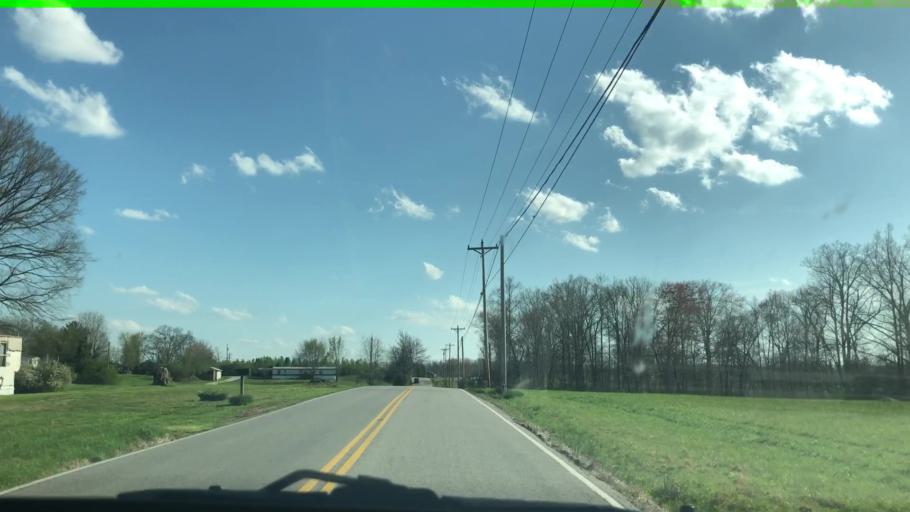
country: US
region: Tennessee
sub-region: Putnam County
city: Baxter
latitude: 36.0852
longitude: -85.5846
